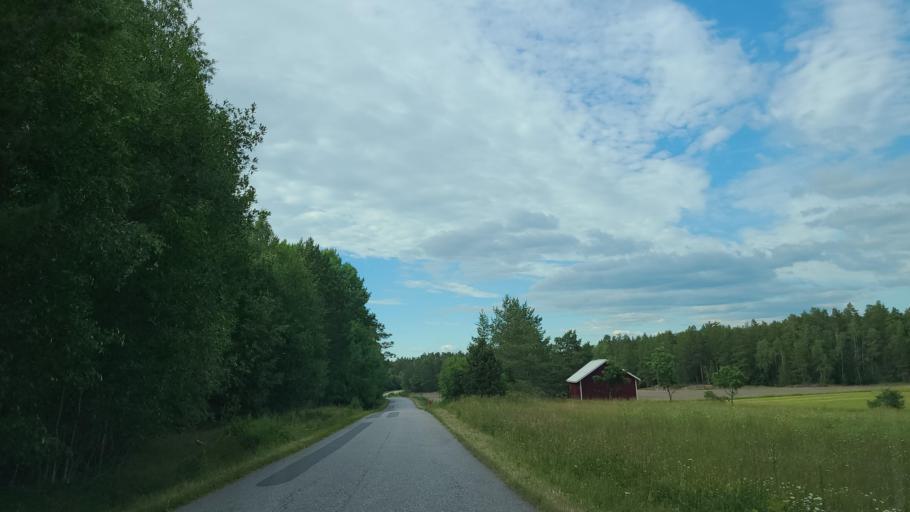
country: FI
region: Varsinais-Suomi
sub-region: Turku
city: Rymaettylae
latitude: 60.3037
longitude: 21.9417
